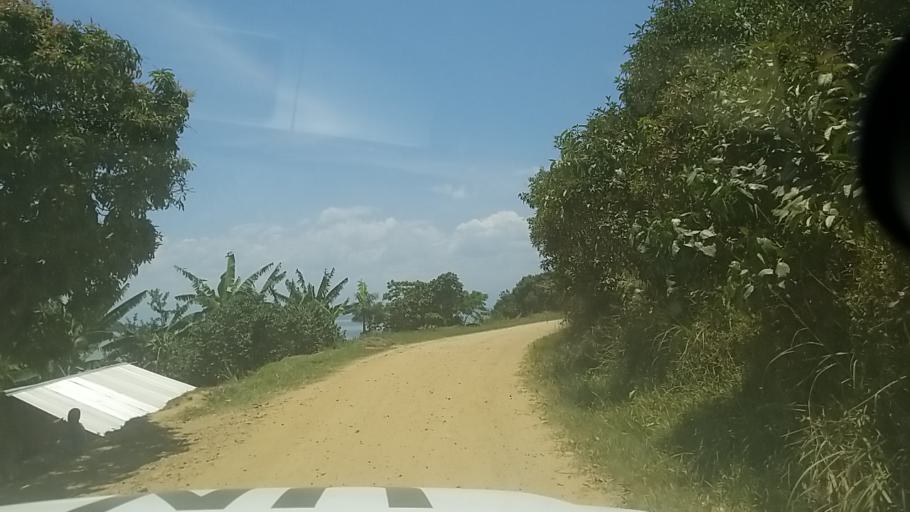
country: CD
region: Nord Kivu
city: Sake
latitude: -1.8443
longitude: 28.9975
